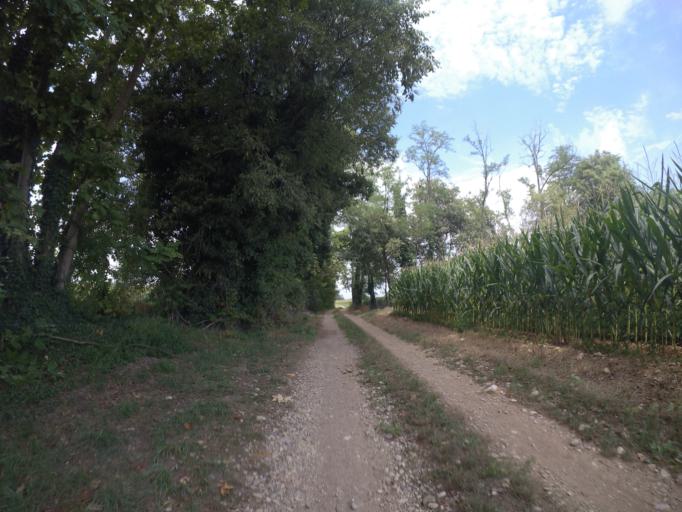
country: IT
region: Friuli Venezia Giulia
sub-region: Provincia di Udine
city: Bertiolo
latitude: 45.9615
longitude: 13.0686
